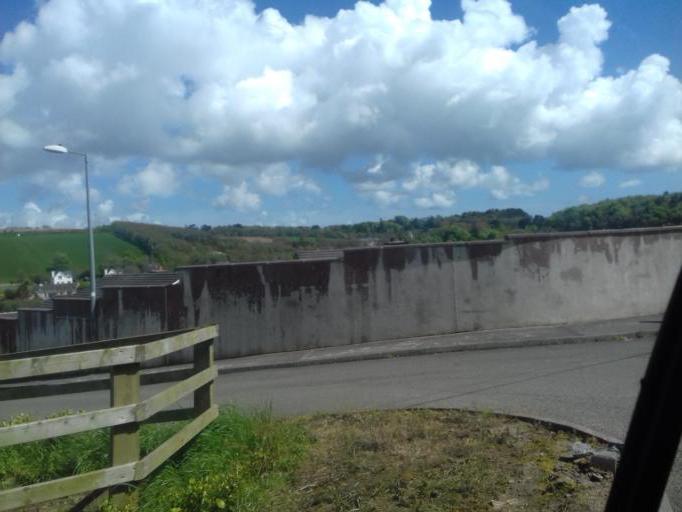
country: IE
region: Munster
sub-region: Waterford
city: Dunmore East
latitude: 52.2446
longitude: -6.9565
